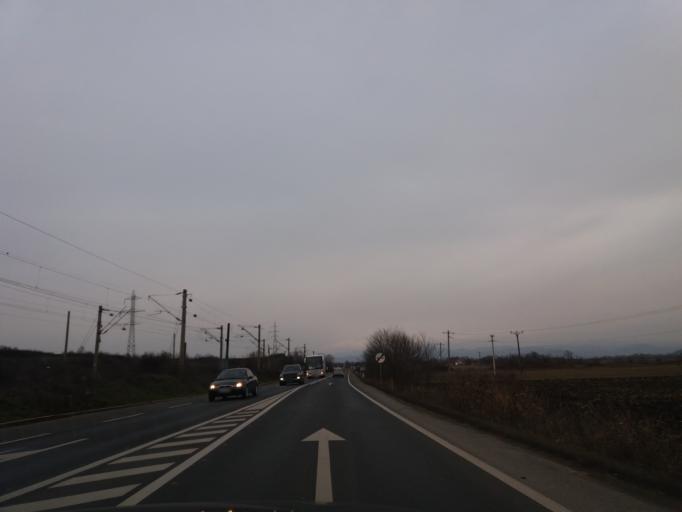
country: RO
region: Hunedoara
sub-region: Comuna Calan
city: Calan
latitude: 45.7647
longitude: 23.0002
